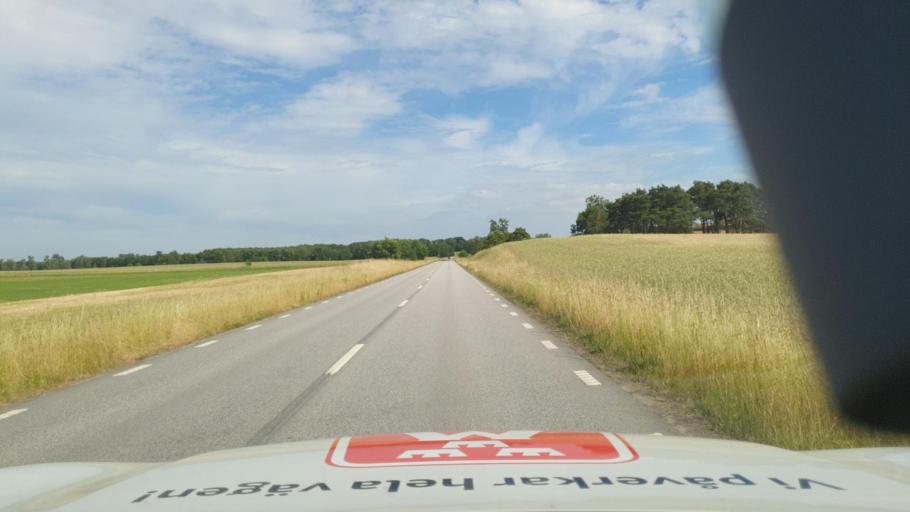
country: SE
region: Skane
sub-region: Sjobo Kommun
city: Blentarp
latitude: 55.6036
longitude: 13.5871
